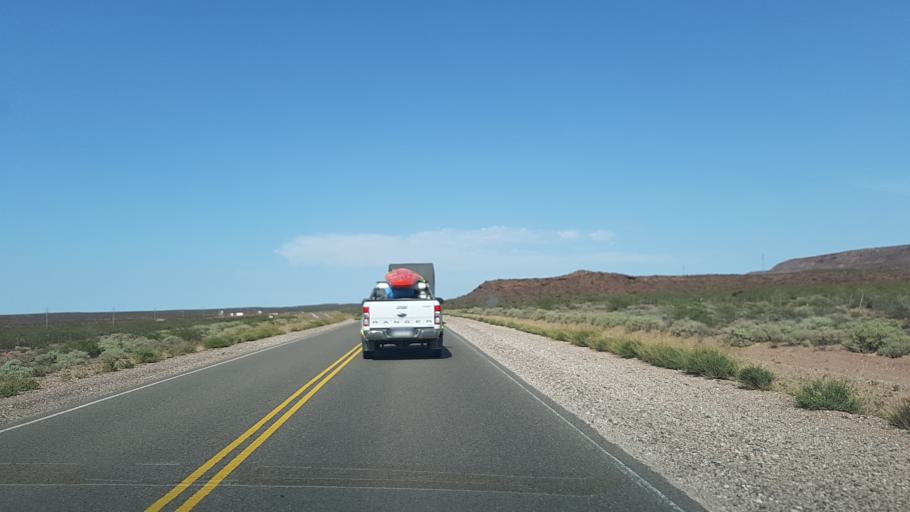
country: AR
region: Neuquen
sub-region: Departamento de Picun Leufu
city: Picun Leufu
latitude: -39.2879
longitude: -68.8753
